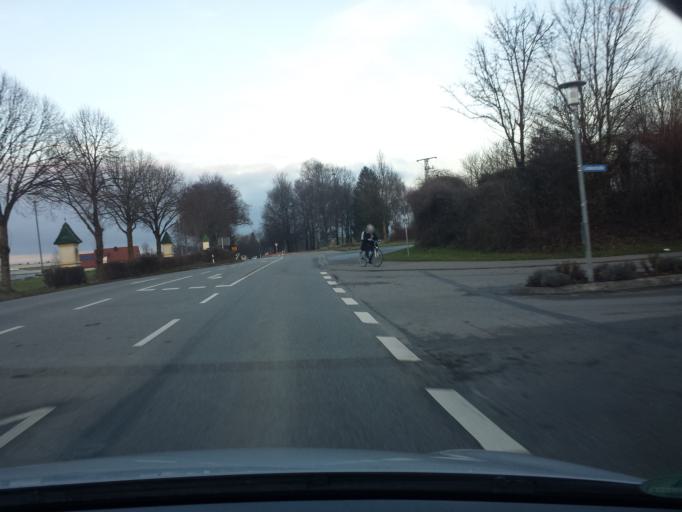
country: DE
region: Baden-Wuerttemberg
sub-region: Tuebingen Region
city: Mittelbiberach
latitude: 48.0901
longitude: 9.7576
